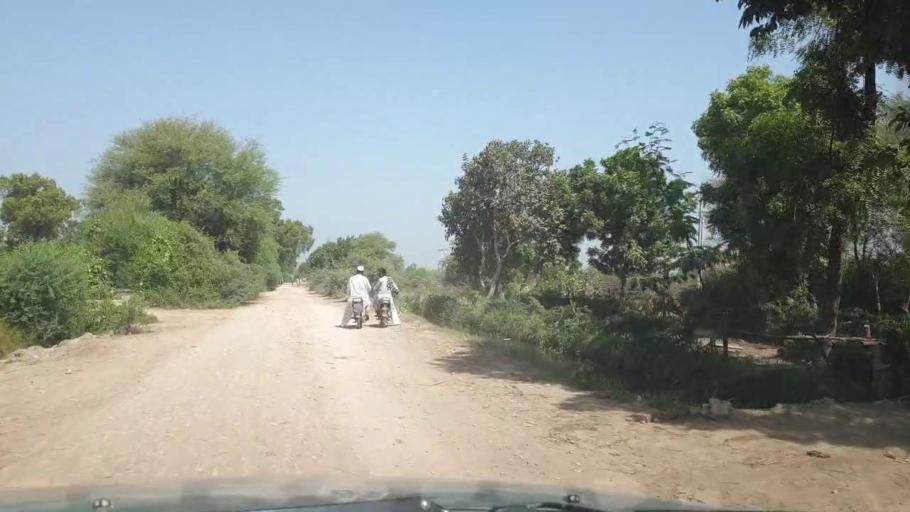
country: PK
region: Sindh
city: Tando Ghulam Ali
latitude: 25.1061
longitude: 68.7663
